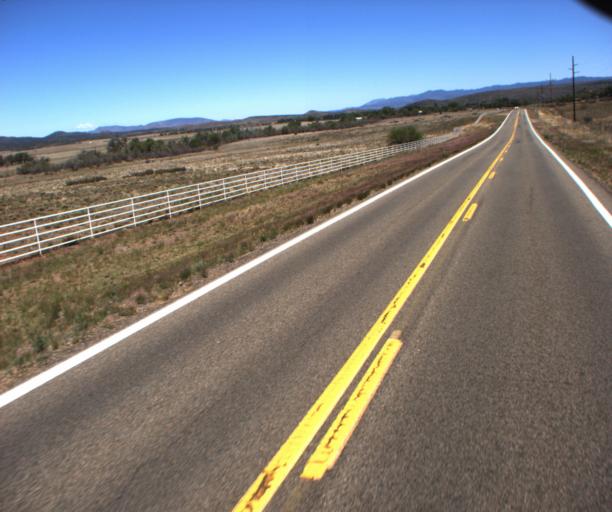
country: US
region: Arizona
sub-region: Yavapai County
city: Congress
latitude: 34.2567
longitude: -112.7319
